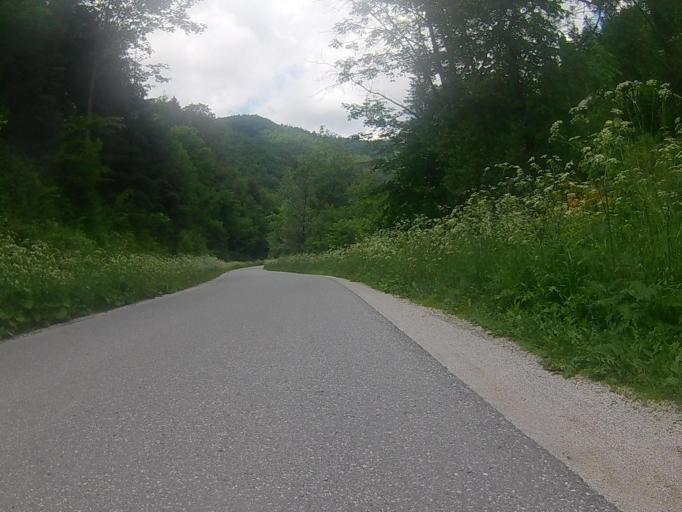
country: SI
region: Maribor
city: Bresternica
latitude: 46.5900
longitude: 15.5577
